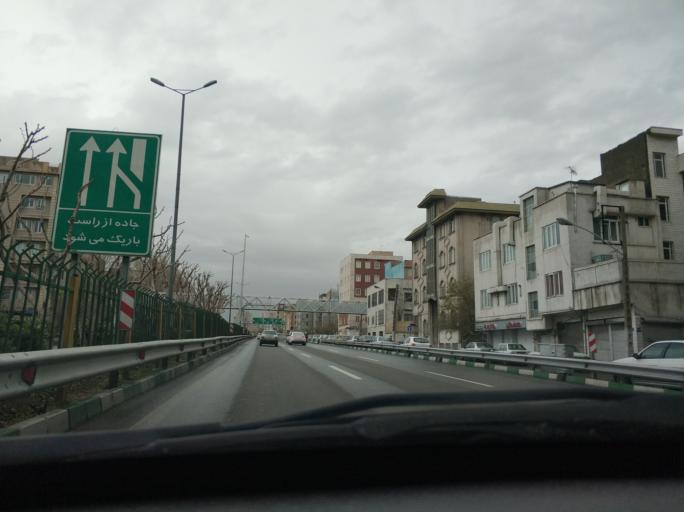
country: IR
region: Tehran
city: Tehran
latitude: 35.7143
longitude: 51.4458
